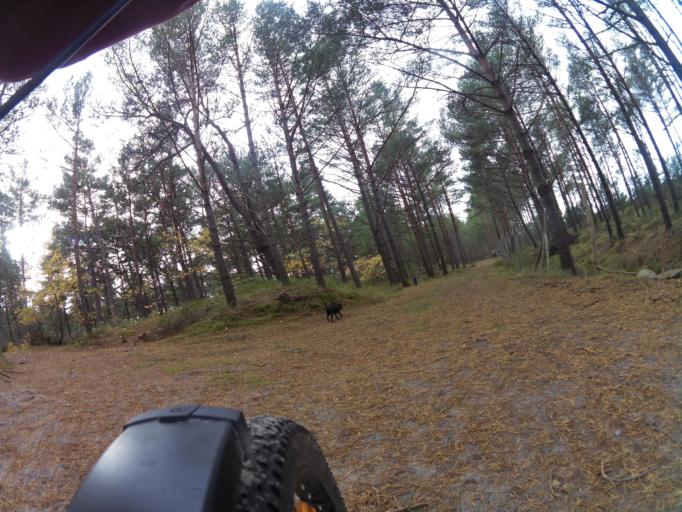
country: PL
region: Pomeranian Voivodeship
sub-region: Powiat wejherowski
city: Choczewo
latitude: 54.8064
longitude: 17.8051
